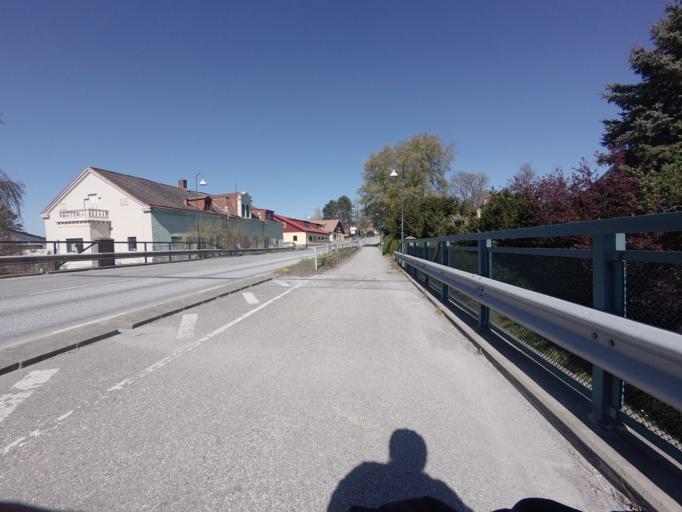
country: SE
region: Skane
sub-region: Kavlinge Kommun
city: Loddekopinge
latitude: 55.7568
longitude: 13.0189
